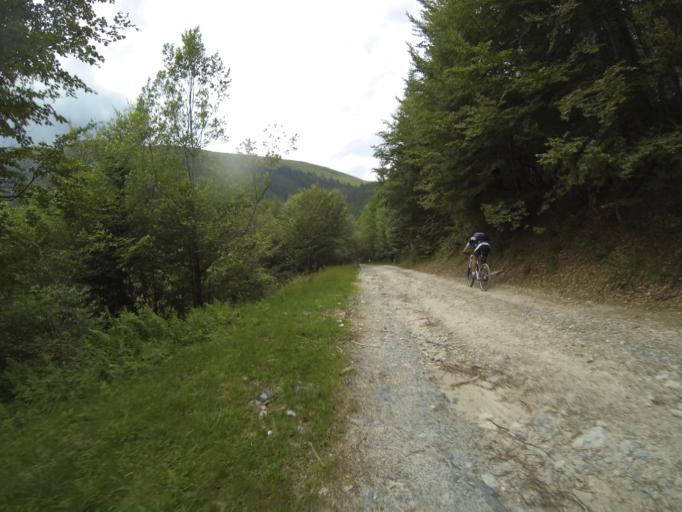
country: RO
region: Gorj
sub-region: Comuna Polovragi
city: Polovragi
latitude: 45.3369
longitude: 23.7919
